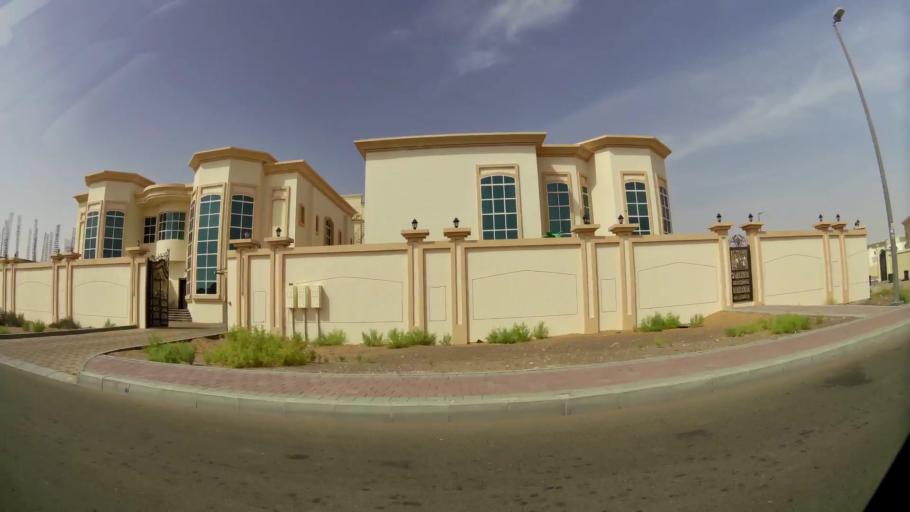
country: AE
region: Abu Dhabi
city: Al Ain
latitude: 24.1735
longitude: 55.6987
